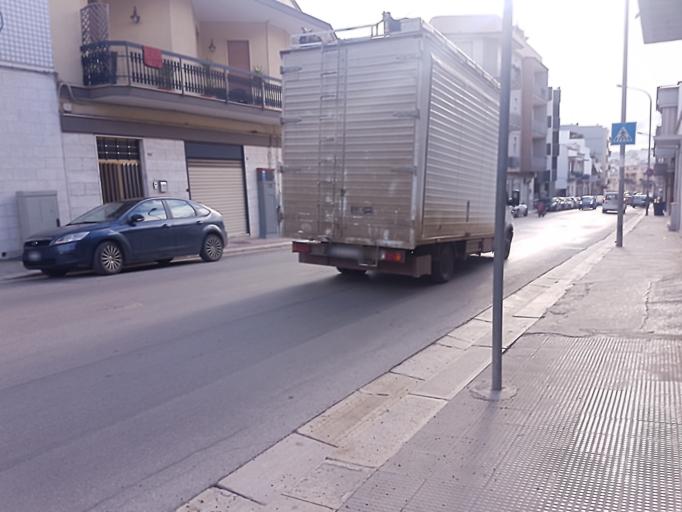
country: IT
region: Apulia
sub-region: Provincia di Barletta - Andria - Trani
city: Andria
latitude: 41.2307
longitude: 16.2875
